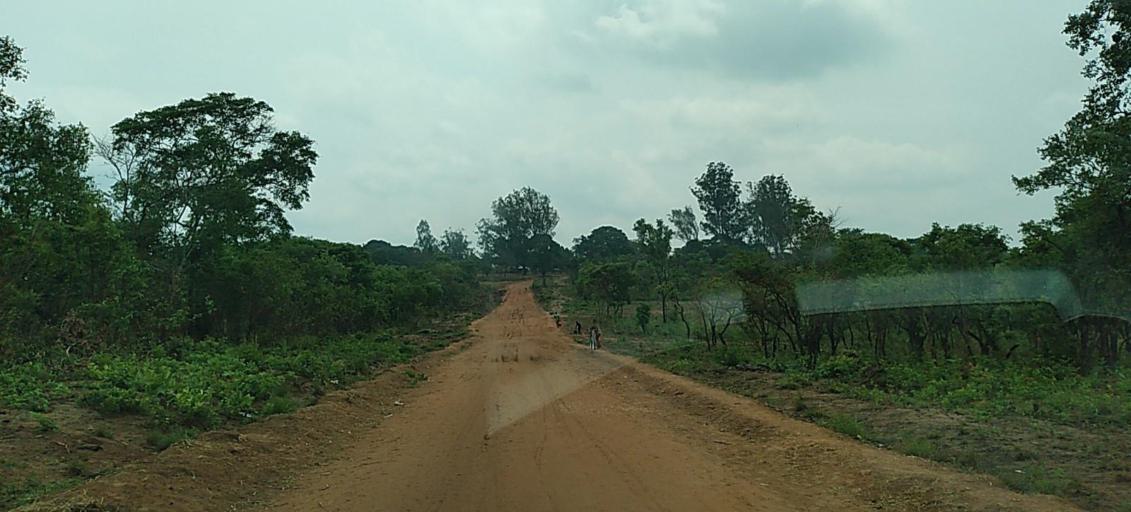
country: ZM
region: North-Western
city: Mwinilunga
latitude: -11.4437
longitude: 24.7478
